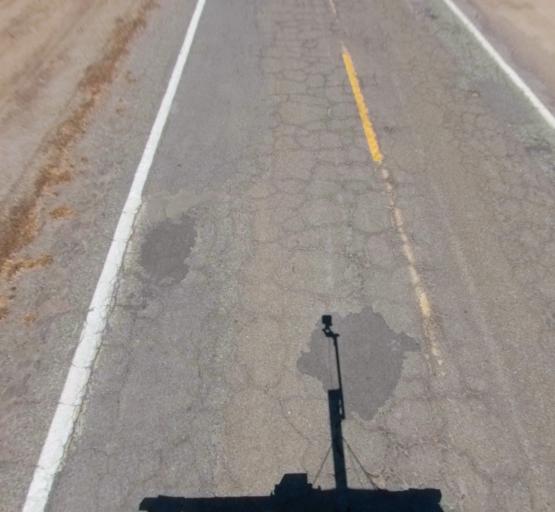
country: US
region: California
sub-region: Madera County
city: Fairmead
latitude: 37.0401
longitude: -120.2674
